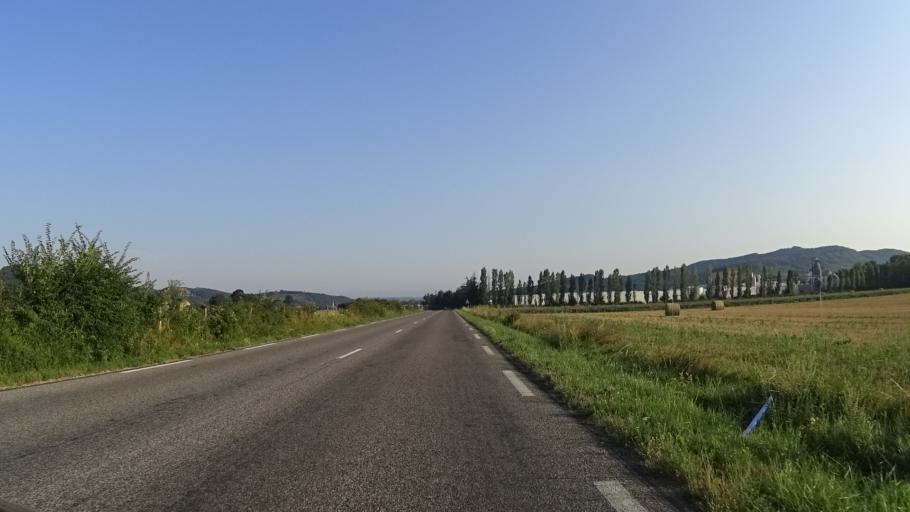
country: FR
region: Midi-Pyrenees
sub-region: Departement de l'Ariege
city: Mirepoix
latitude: 43.0430
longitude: 1.8961
